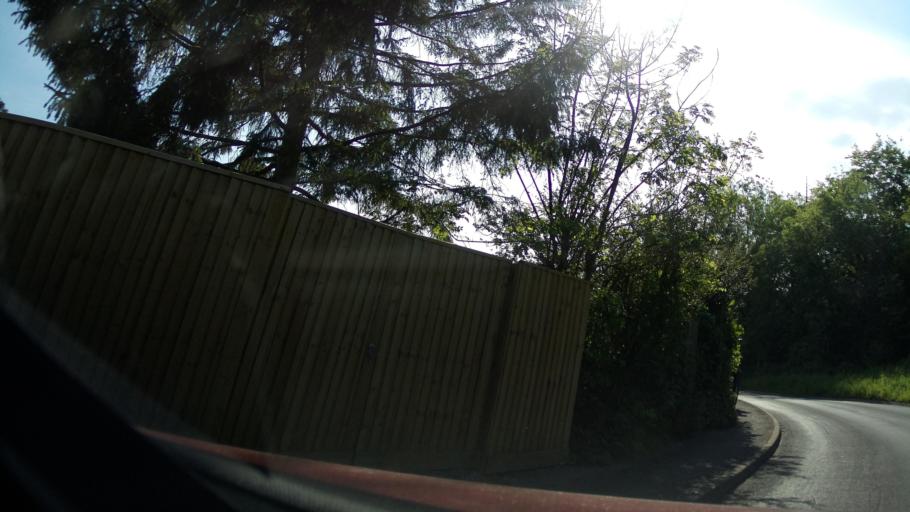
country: GB
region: England
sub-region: Wiltshire
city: Chippenham
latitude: 51.4723
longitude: -2.1212
